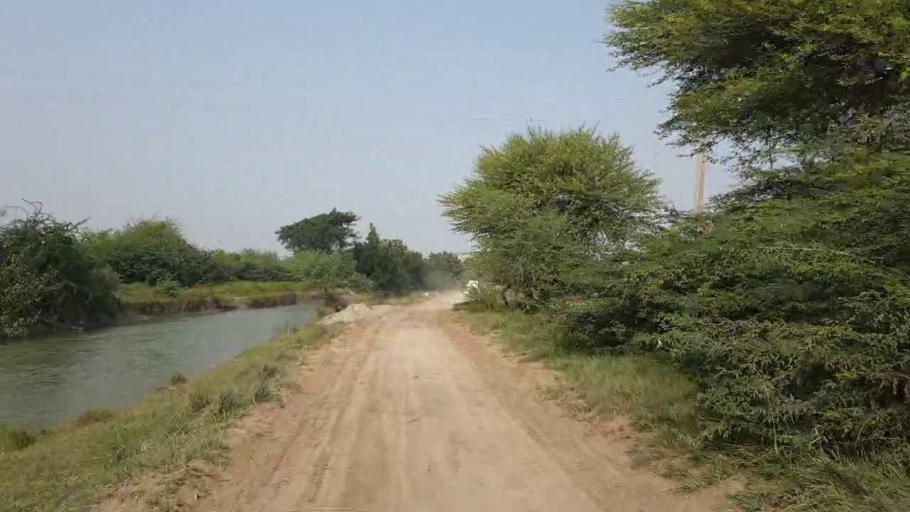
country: PK
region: Sindh
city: Kario
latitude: 24.8319
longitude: 68.5451
